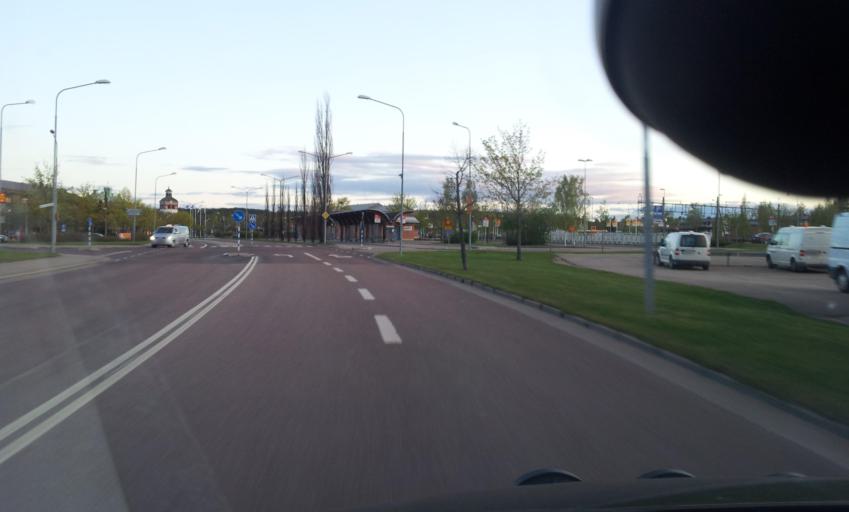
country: SE
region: Gaevleborg
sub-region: Bollnas Kommun
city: Bollnas
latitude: 61.3520
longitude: 16.3953
